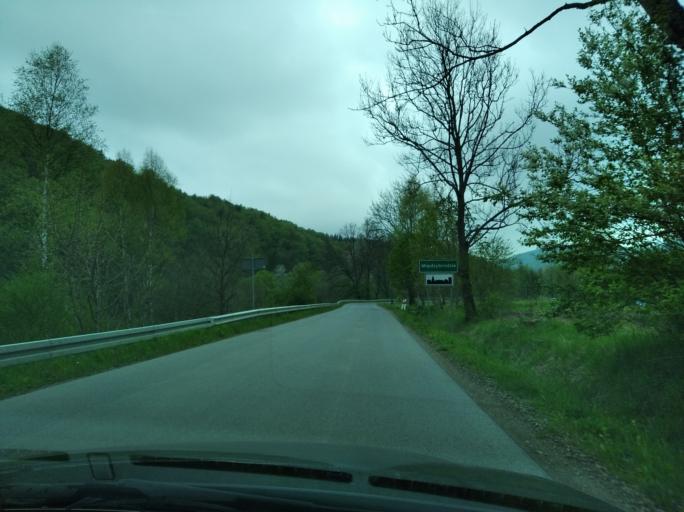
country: PL
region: Subcarpathian Voivodeship
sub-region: Powiat sanocki
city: Sanok
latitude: 49.5964
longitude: 22.2143
